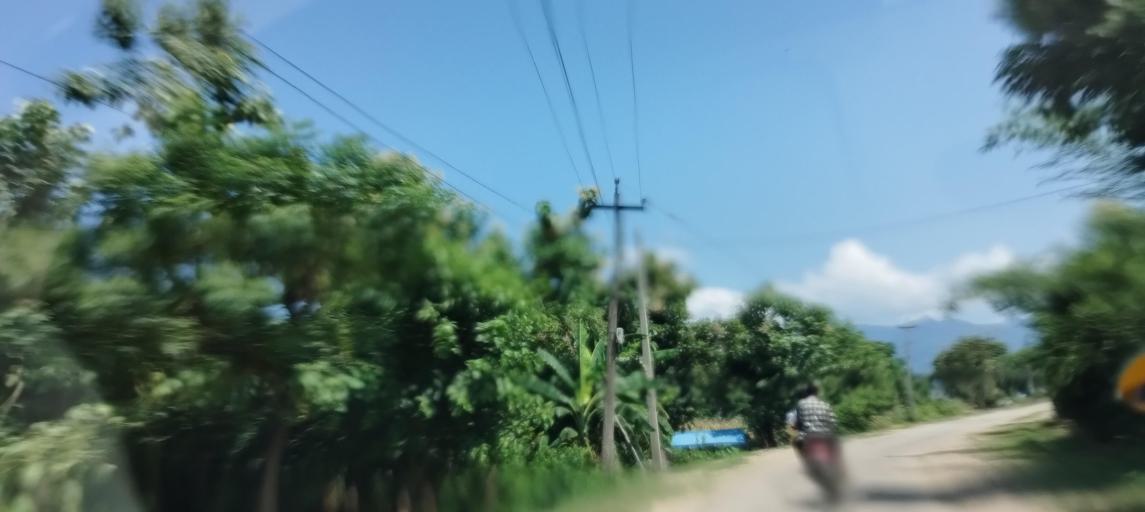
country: NP
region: Far Western
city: Tikapur
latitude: 28.5078
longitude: 81.3032
